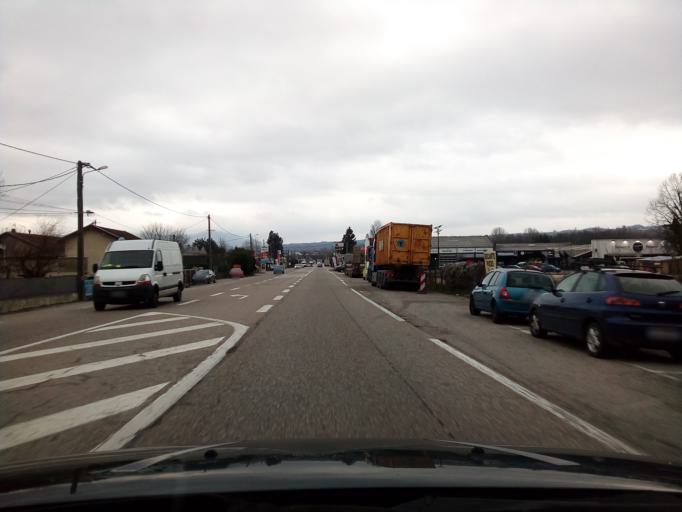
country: FR
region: Rhone-Alpes
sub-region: Departement de l'Isere
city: Saint-Jean-de-Moirans
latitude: 45.3262
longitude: 5.5819
